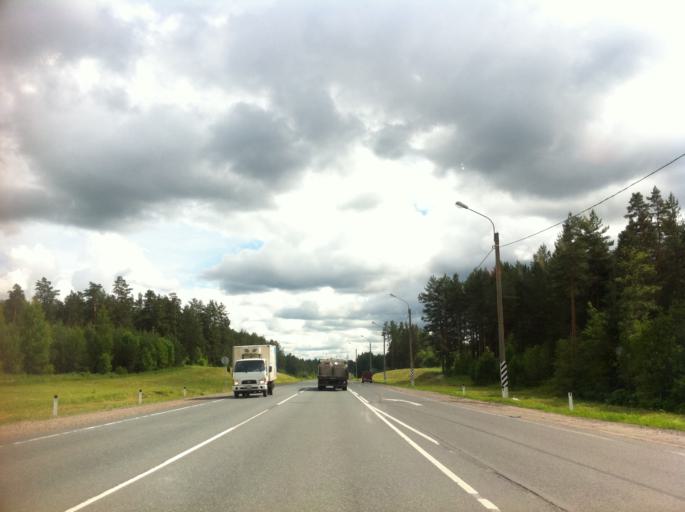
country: RU
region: Leningrad
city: Luga
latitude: 58.7131
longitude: 29.8792
